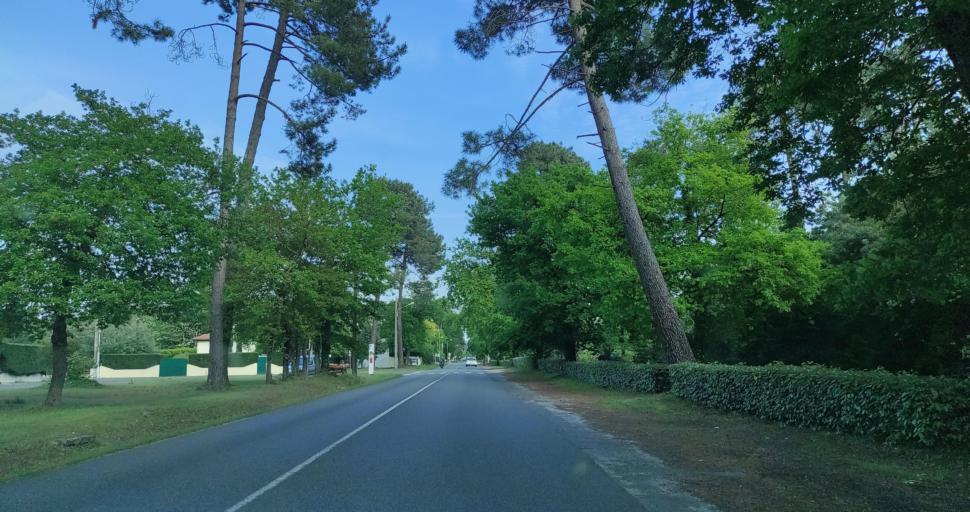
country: FR
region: Aquitaine
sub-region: Departement de la Gironde
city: Ares
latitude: 44.7610
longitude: -1.1274
